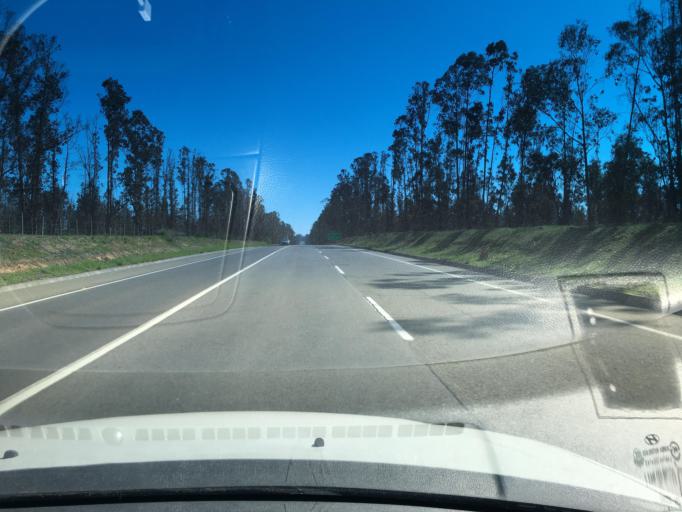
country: CL
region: Valparaiso
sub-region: San Antonio Province
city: El Tabo
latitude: -33.4068
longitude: -71.5597
